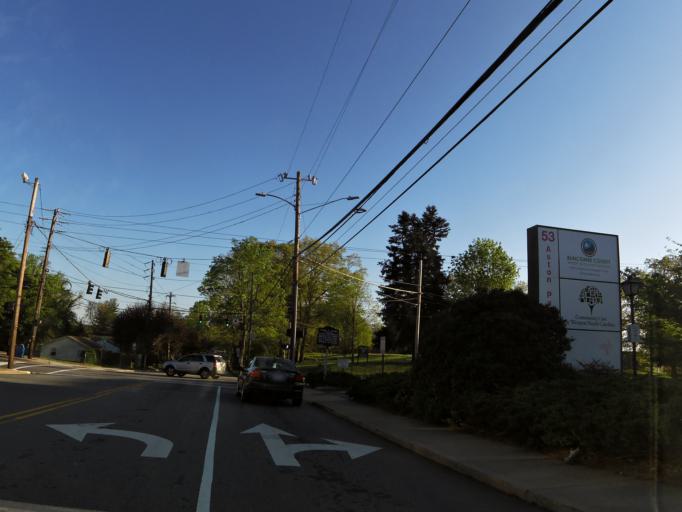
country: US
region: North Carolina
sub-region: Buncombe County
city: Asheville
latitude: 35.5915
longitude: -82.5590
